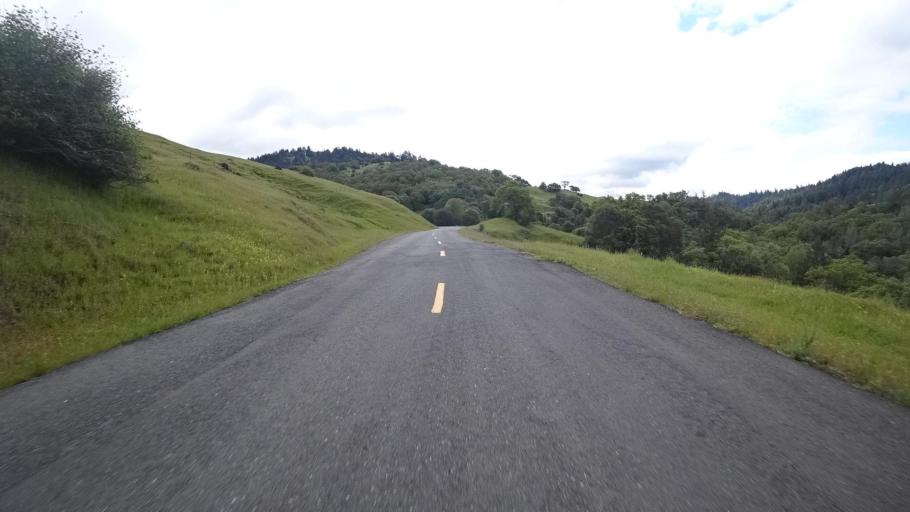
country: US
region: California
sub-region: Humboldt County
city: Redway
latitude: 40.2068
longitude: -123.5950
